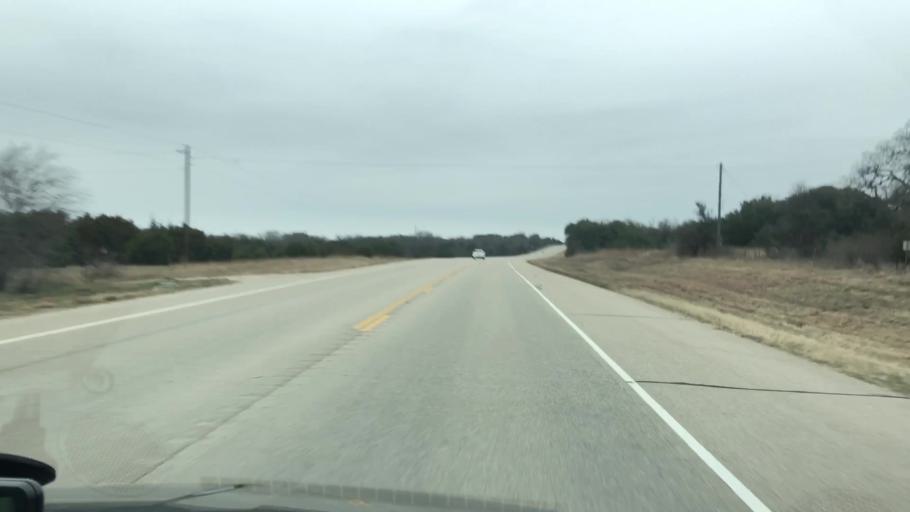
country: US
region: Texas
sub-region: Hamilton County
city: Hamilton
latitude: 31.8355
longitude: -98.1154
